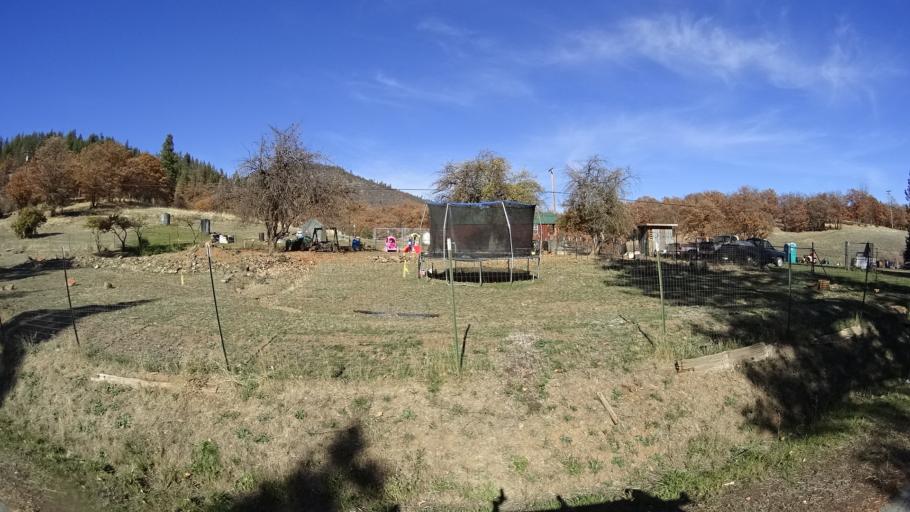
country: US
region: California
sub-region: Siskiyou County
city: Yreka
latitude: 41.7222
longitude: -122.6931
